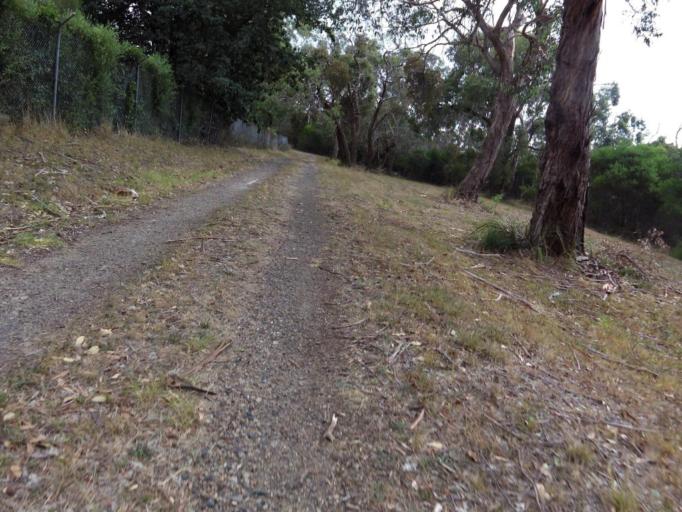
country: AU
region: Victoria
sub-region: Frankston
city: Frankston South
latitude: -38.1830
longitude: 145.1291
